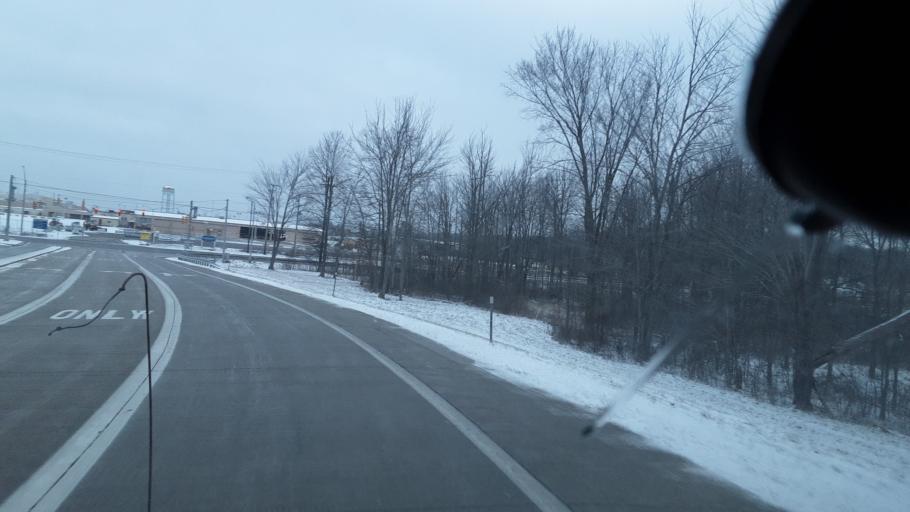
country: US
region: Ohio
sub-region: Trumbull County
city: Lordstown
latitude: 41.1420
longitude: -80.8665
